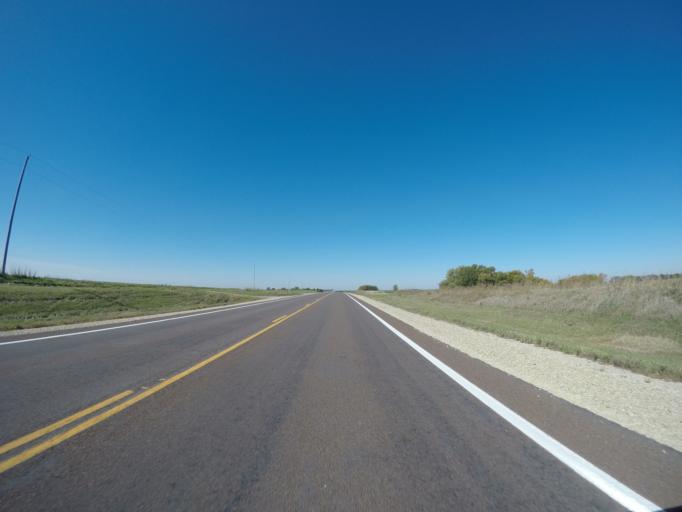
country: US
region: Kansas
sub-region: Riley County
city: Fort Riley North
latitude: 39.3065
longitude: -96.8739
